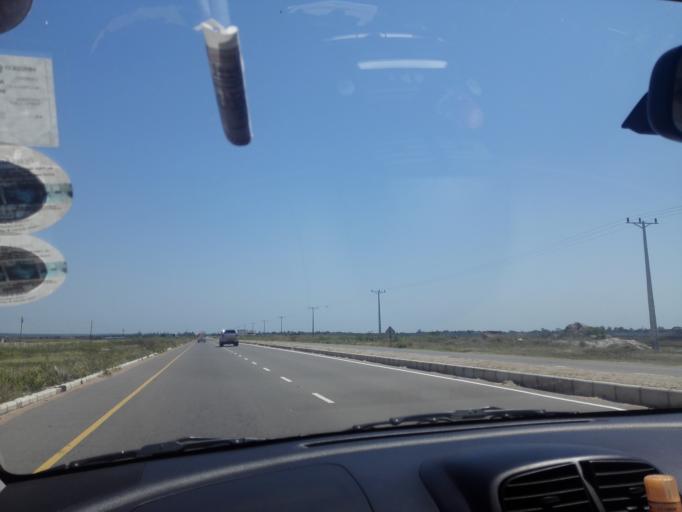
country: MZ
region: Maputo City
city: Maputo
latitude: -25.8349
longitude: 32.6719
